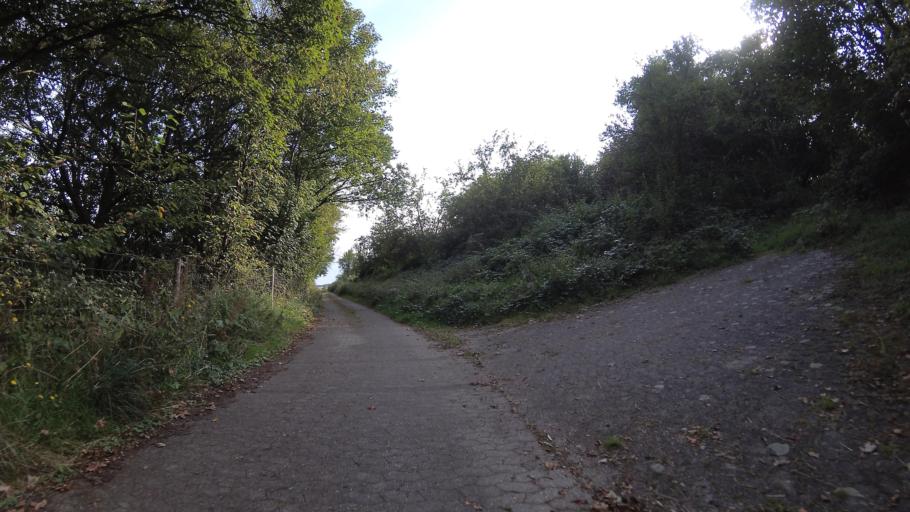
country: DE
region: Saarland
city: Freisen
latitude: 49.4953
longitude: 7.2407
